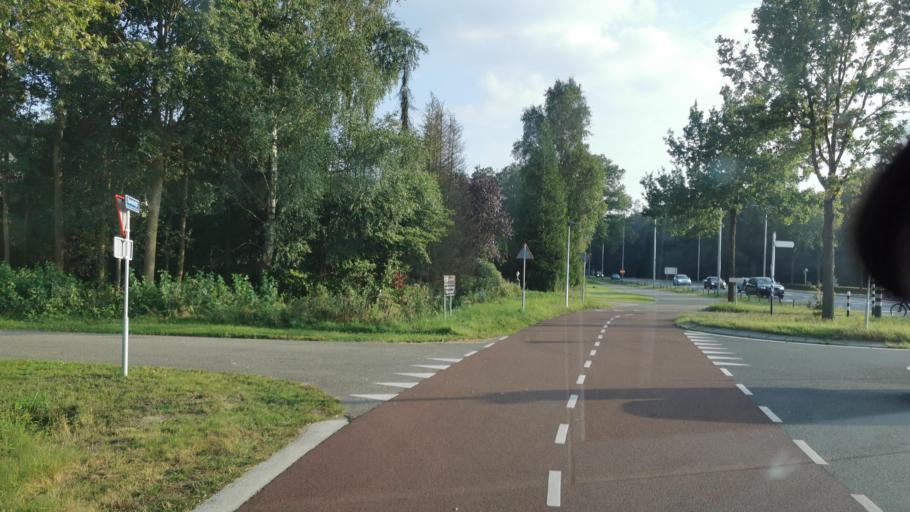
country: NL
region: Overijssel
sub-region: Gemeente Oldenzaal
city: Oldenzaal
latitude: 52.2847
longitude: 6.9301
